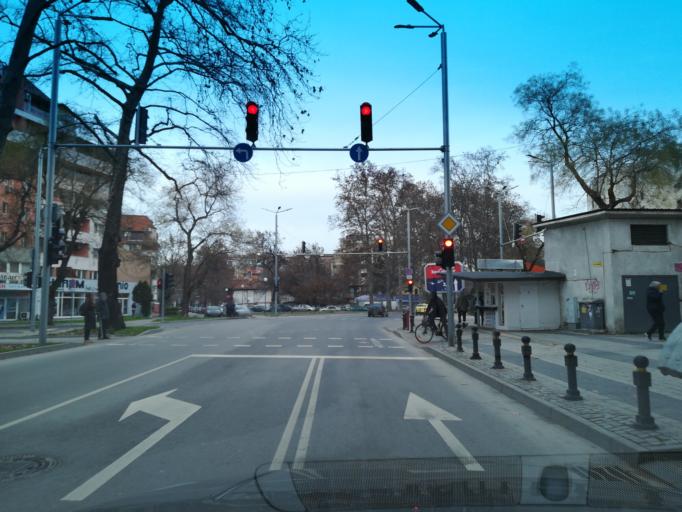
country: BG
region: Plovdiv
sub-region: Obshtina Plovdiv
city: Plovdiv
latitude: 42.1455
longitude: 24.7315
